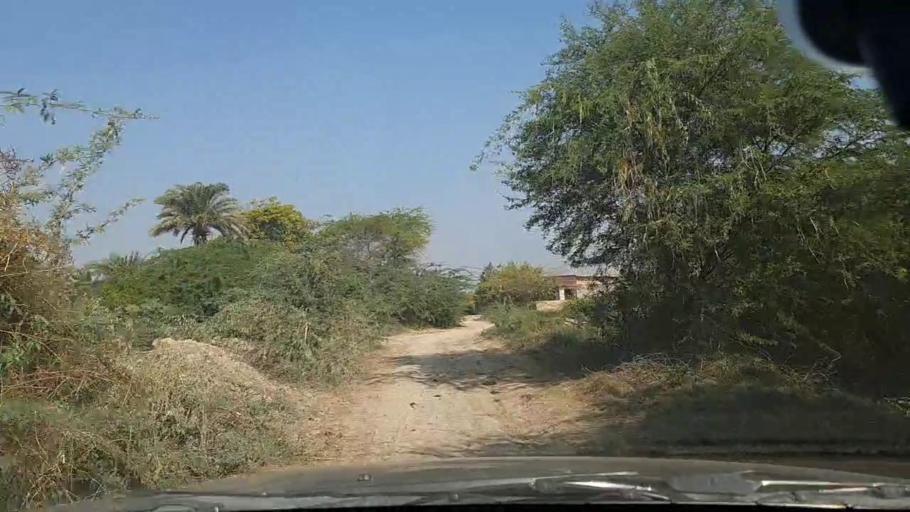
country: PK
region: Sindh
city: Chuhar Jamali
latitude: 24.5179
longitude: 67.8865
